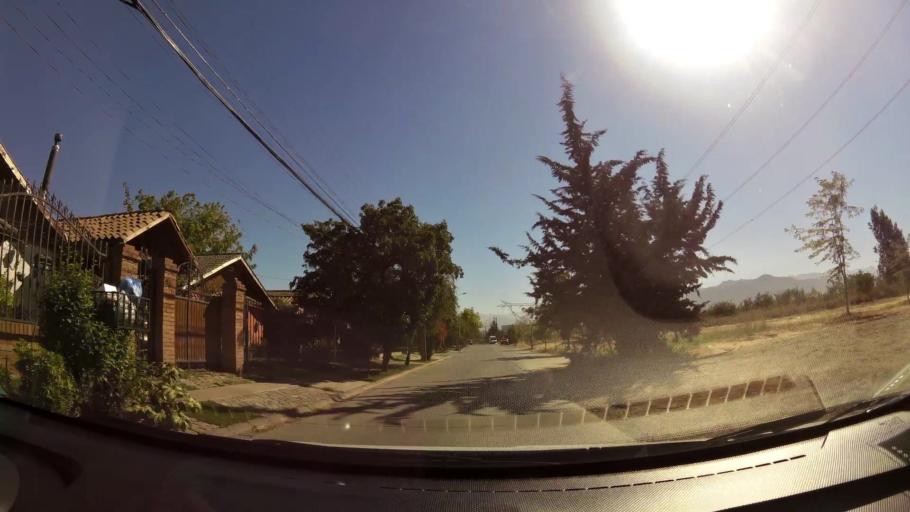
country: CL
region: O'Higgins
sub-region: Provincia de Cachapoal
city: Rancagua
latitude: -34.1806
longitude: -70.7050
